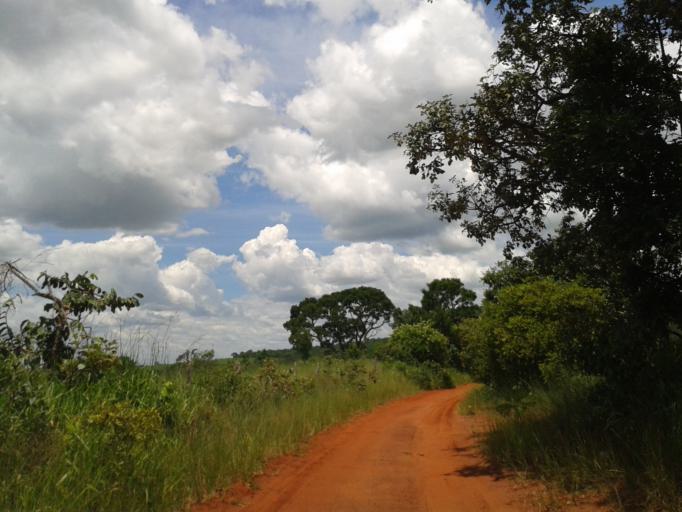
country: BR
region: Minas Gerais
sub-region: Ituiutaba
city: Ituiutaba
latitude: -18.8479
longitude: -49.5053
